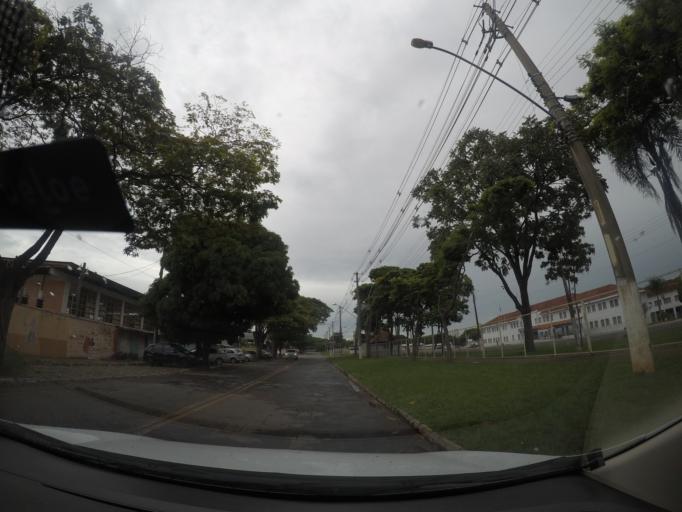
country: BR
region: Goias
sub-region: Goiania
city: Goiania
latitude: -16.6851
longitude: -49.2362
